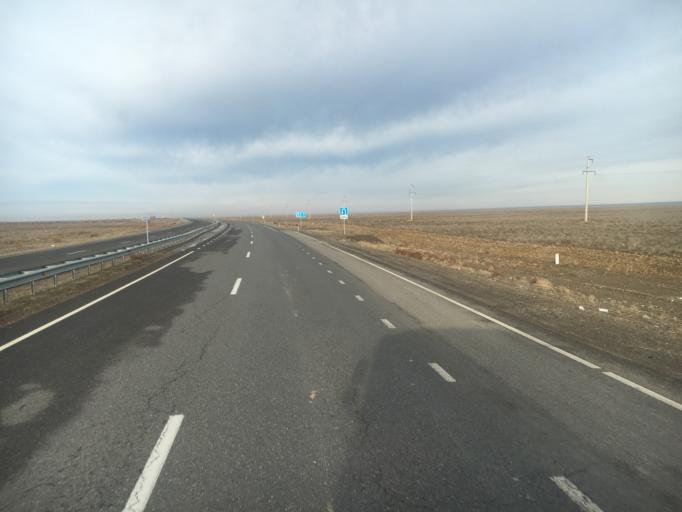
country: KZ
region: Ongtustik Qazaqstan
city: Turkestan
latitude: 43.5007
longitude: 67.8450
